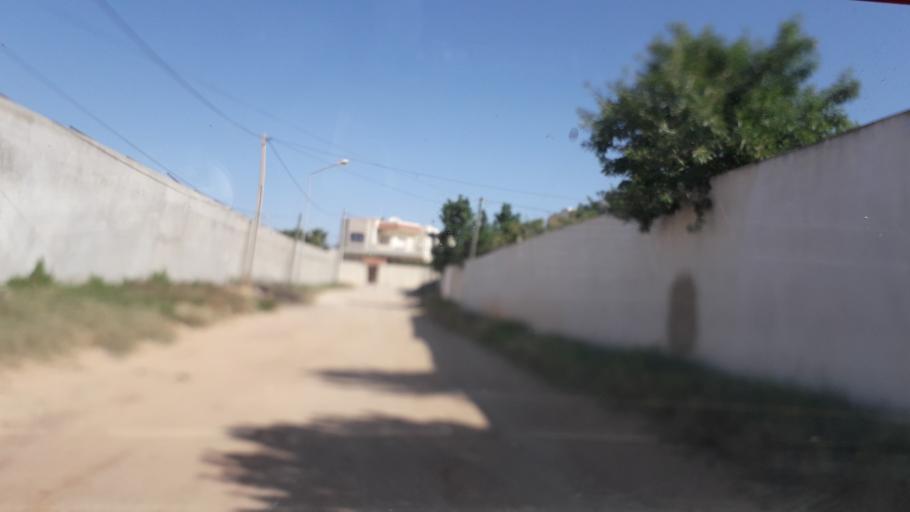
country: TN
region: Safaqis
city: Al Qarmadah
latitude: 34.8080
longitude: 10.7639
